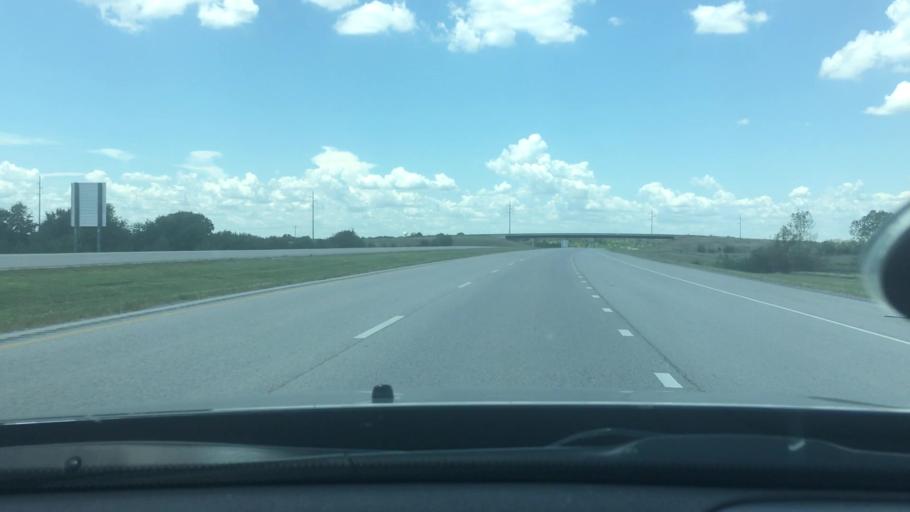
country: US
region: Oklahoma
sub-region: Bryan County
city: Calera
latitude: 33.9731
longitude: -96.4217
